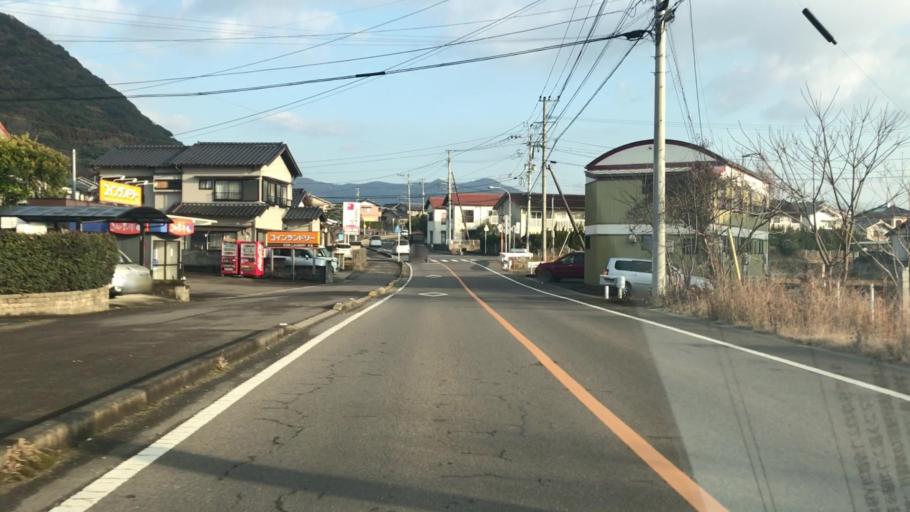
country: JP
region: Saga Prefecture
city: Takeocho-takeo
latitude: 33.2039
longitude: 130.0247
